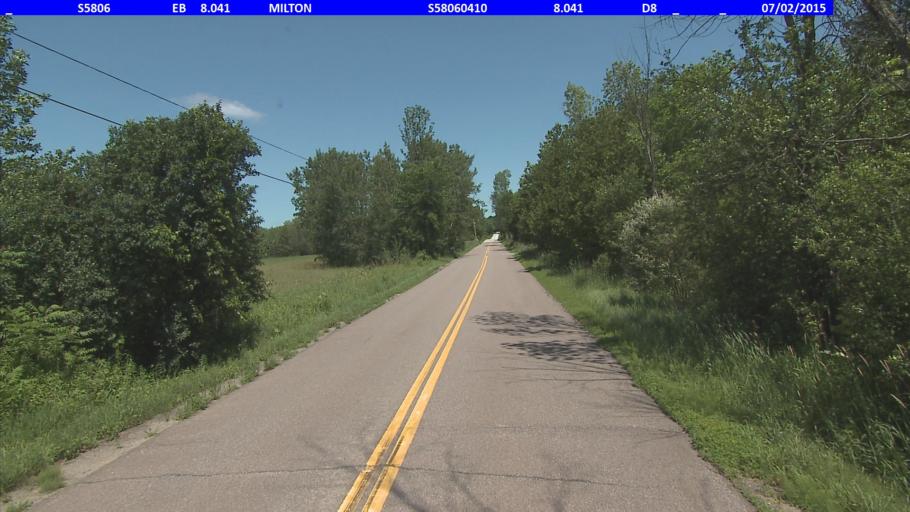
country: US
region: Vermont
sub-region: Chittenden County
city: Milton
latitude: 44.7118
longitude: -73.2045
